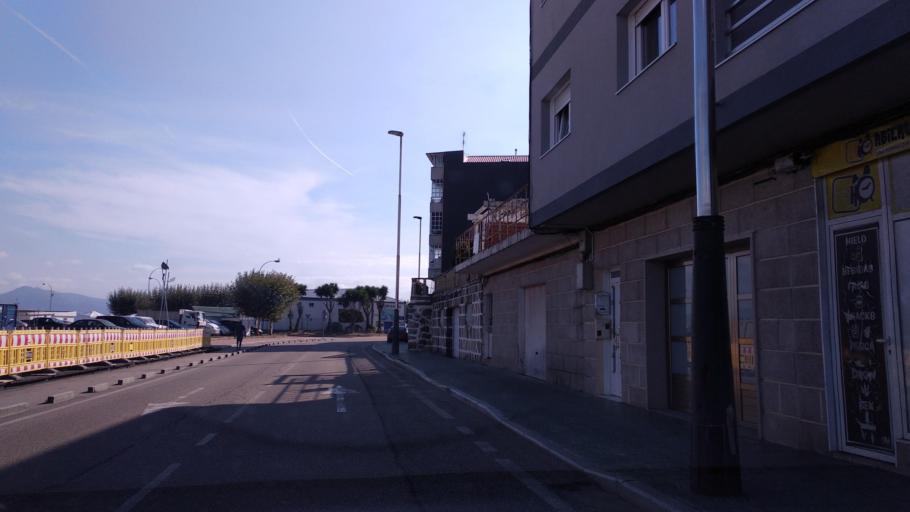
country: ES
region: Galicia
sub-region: Provincia de Pontevedra
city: Moana
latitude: 42.2752
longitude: -8.7365
